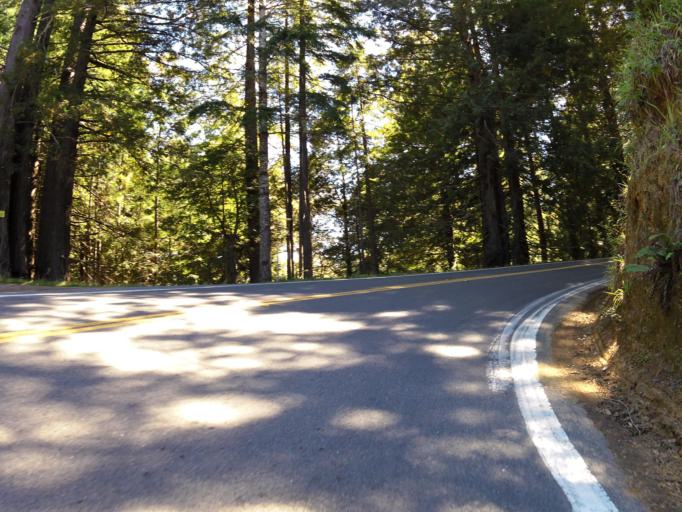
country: US
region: California
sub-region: Mendocino County
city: Fort Bragg
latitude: 39.7248
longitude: -123.8091
